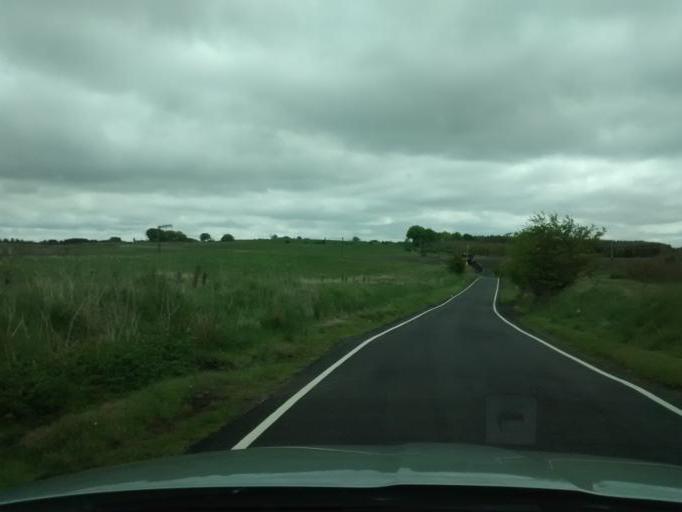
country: GB
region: Scotland
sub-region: West Lothian
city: Armadale
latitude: 55.8855
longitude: -3.7218
